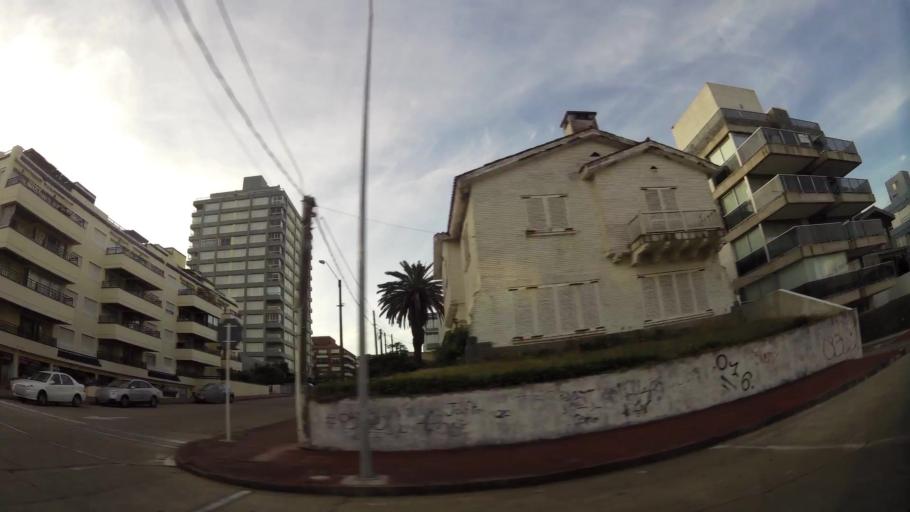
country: UY
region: Maldonado
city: Punta del Este
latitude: -34.9644
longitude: -54.9427
